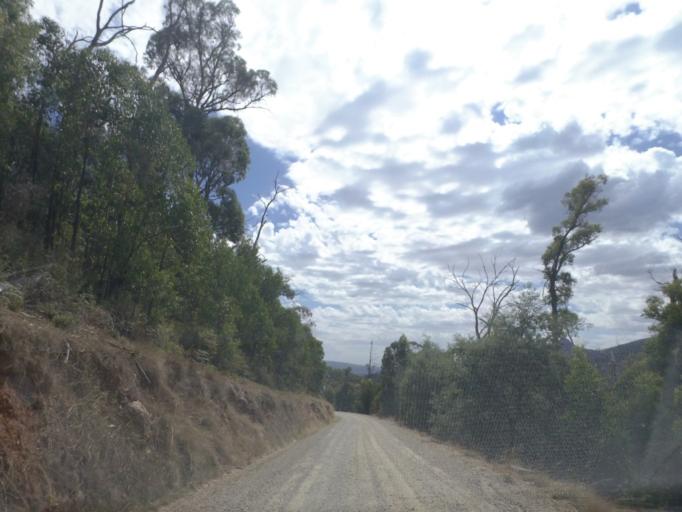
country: AU
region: Victoria
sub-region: Murrindindi
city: Alexandra
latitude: -37.4568
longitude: 145.7605
